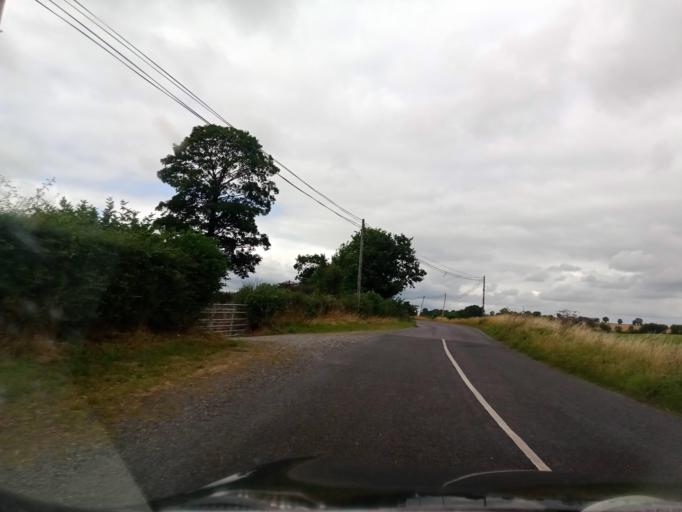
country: IE
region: Leinster
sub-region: Laois
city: Stradbally
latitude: 52.9801
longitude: -7.1810
